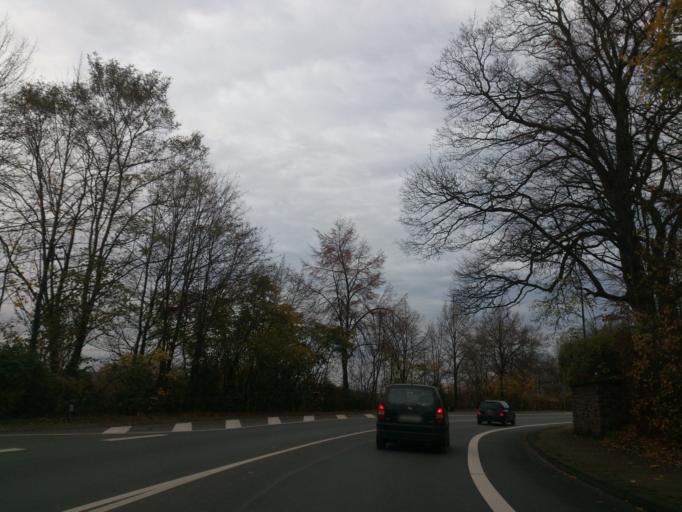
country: DE
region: North Rhine-Westphalia
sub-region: Regierungsbezirk Detmold
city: Hoexter
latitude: 51.7699
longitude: 9.3789
